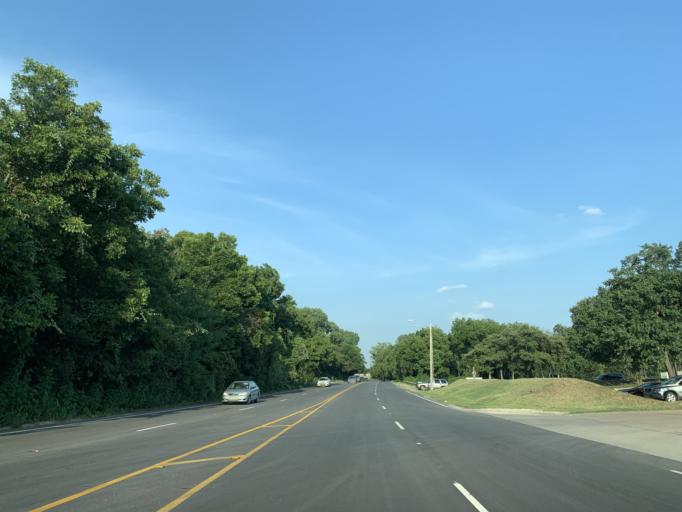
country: US
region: Texas
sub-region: Tarrant County
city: Hurst
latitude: 32.8022
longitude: -97.1810
